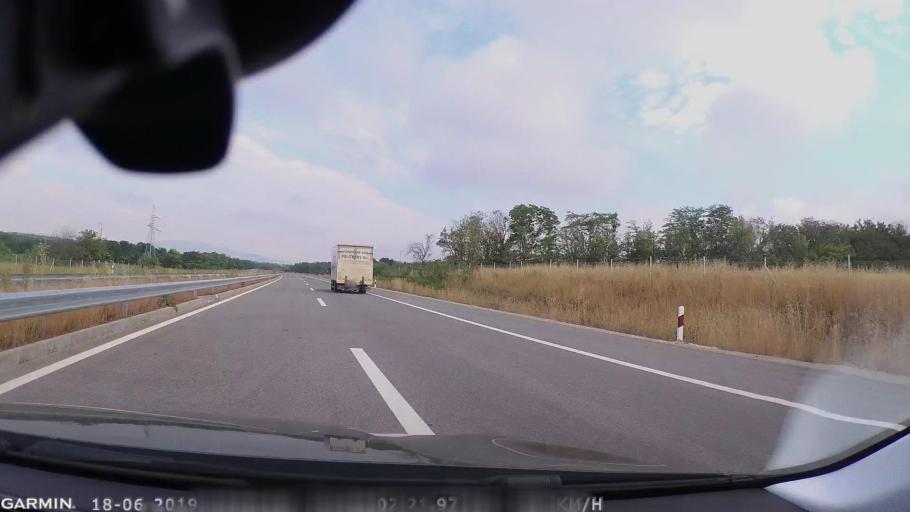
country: MK
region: Sveti Nikole
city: Sveti Nikole
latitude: 41.8447
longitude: 21.9759
